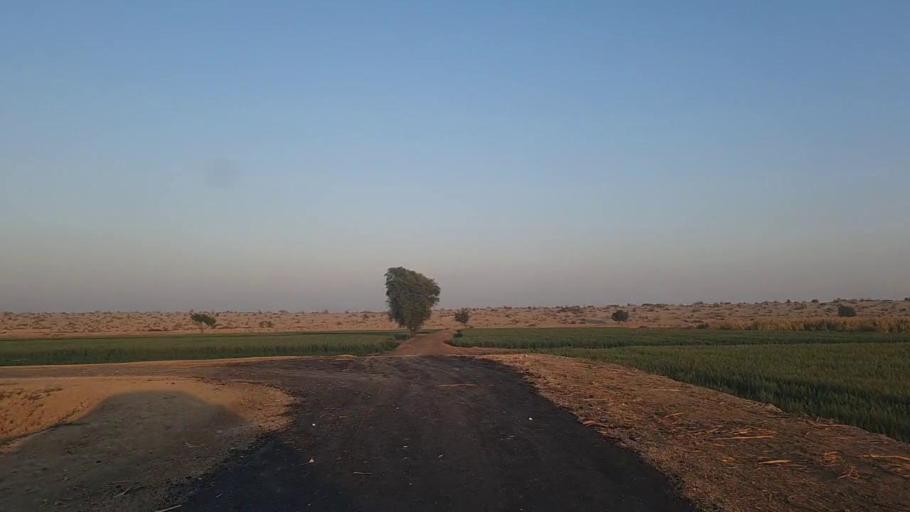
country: PK
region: Sindh
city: Jam Sahib
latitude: 26.3639
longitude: 68.7214
